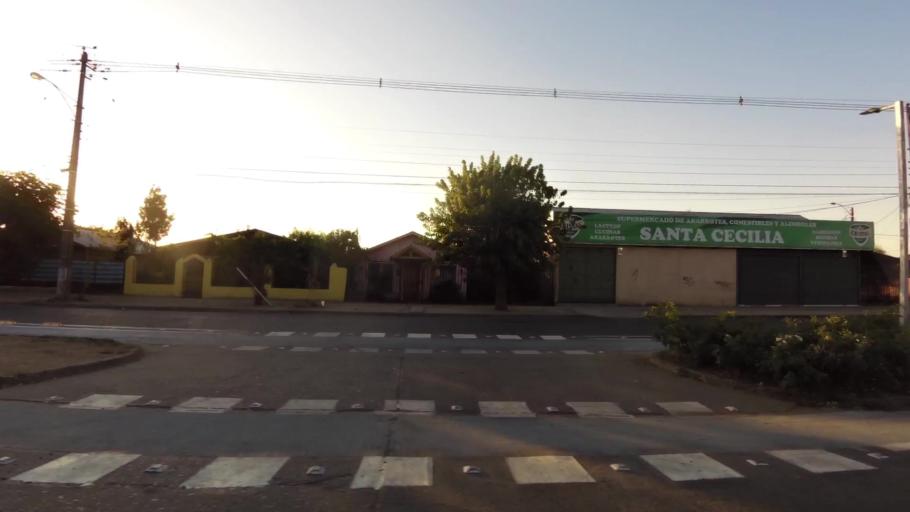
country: CL
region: Maule
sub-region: Provincia de Talca
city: Talca
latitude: -35.4475
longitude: -71.6557
